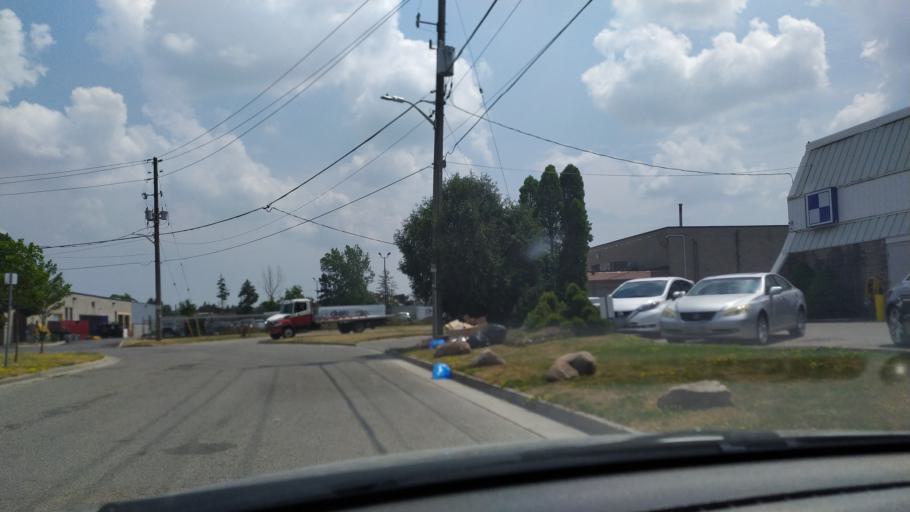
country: CA
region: Ontario
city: London
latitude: 42.9879
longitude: -81.1708
